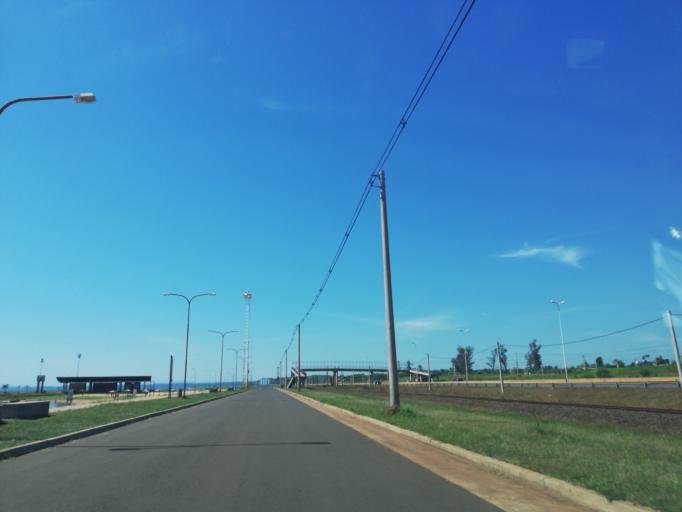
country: AR
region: Misiones
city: Garupa
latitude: -27.4310
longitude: -55.8660
